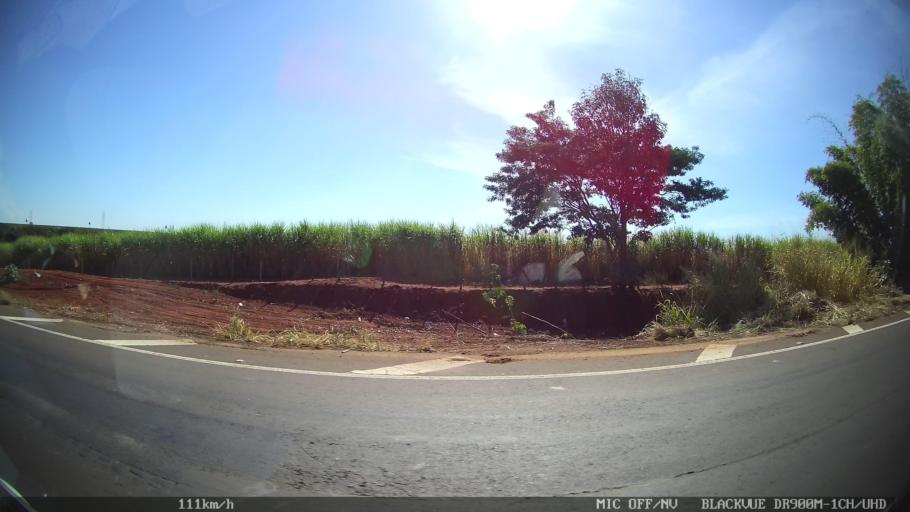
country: BR
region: Sao Paulo
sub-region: Olimpia
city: Olimpia
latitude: -20.6376
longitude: -48.8222
